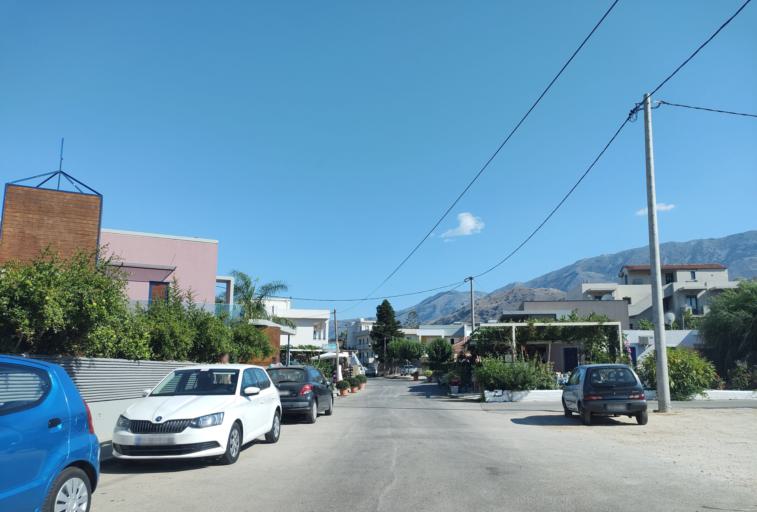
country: GR
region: Crete
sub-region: Nomos Chanias
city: Georgioupolis
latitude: 35.3615
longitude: 24.2612
